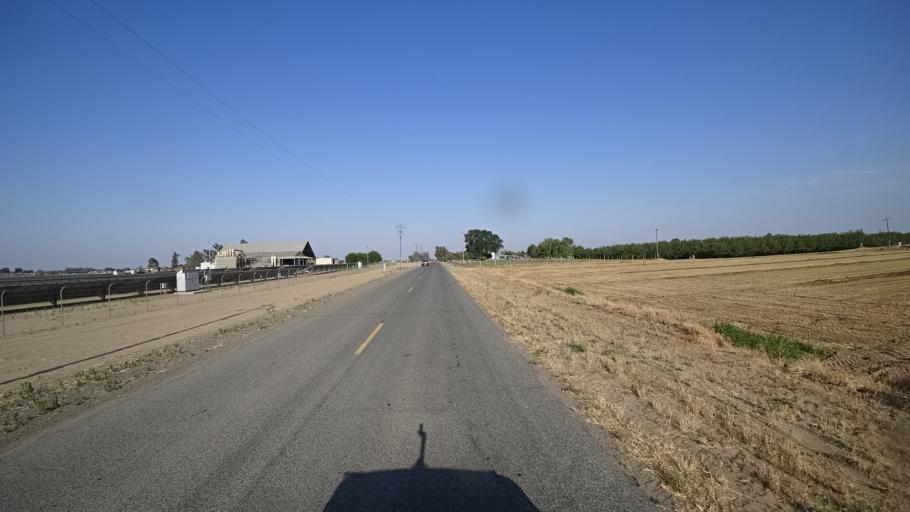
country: US
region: California
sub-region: Fresno County
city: Riverdale
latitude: 36.3803
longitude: -119.8208
